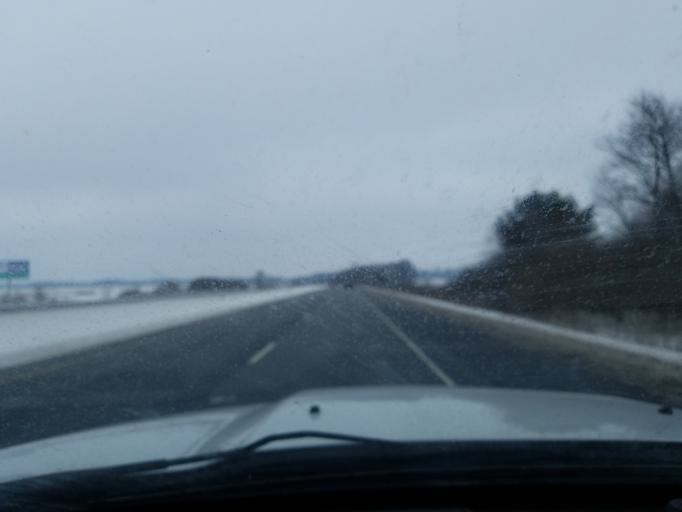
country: US
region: Indiana
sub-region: Marshall County
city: Argos
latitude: 41.2433
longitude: -86.2613
